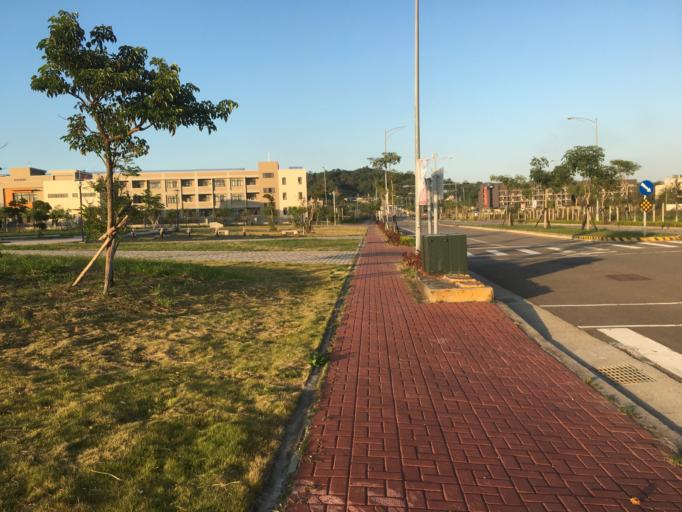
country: TW
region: Taiwan
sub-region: Miaoli
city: Miaoli
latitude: 24.6089
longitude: 120.8270
